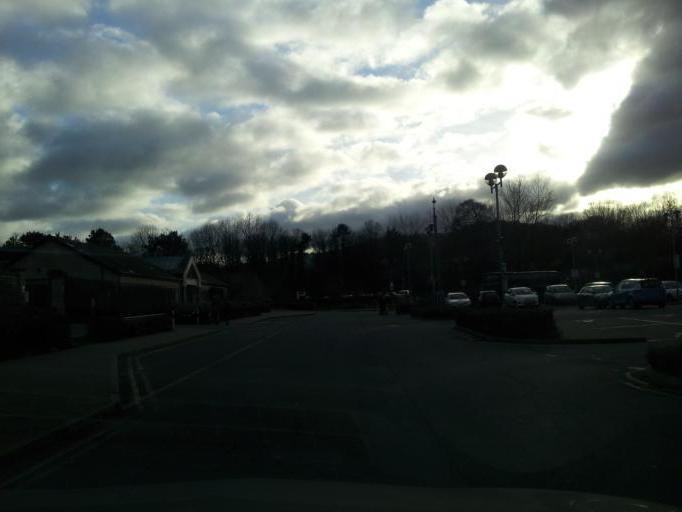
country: GB
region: England
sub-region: Derbyshire
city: Bakewell
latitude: 53.1913
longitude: -1.6152
